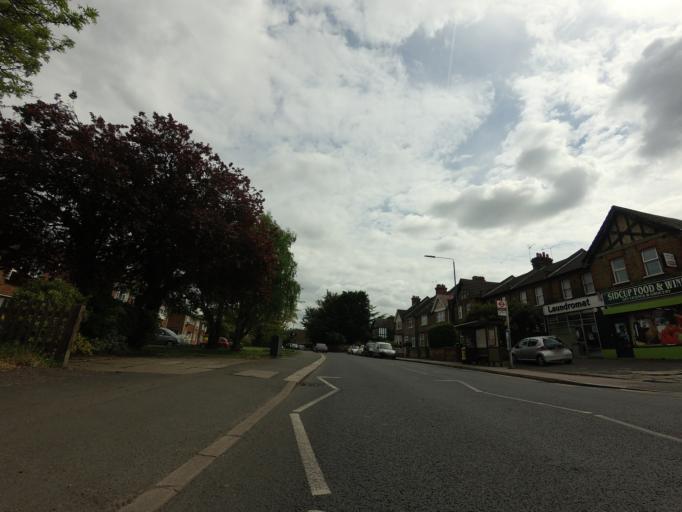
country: GB
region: England
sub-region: Greater London
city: Sidcup
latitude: 51.4289
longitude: 0.0889
